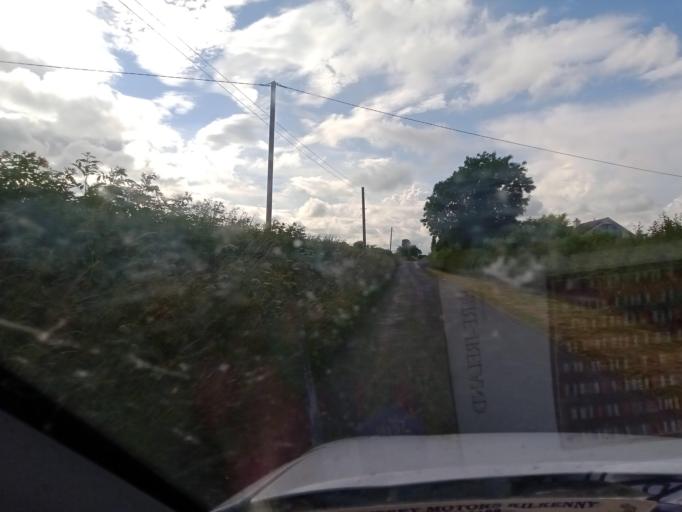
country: IE
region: Leinster
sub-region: Laois
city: Rathdowney
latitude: 52.7861
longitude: -7.5508
